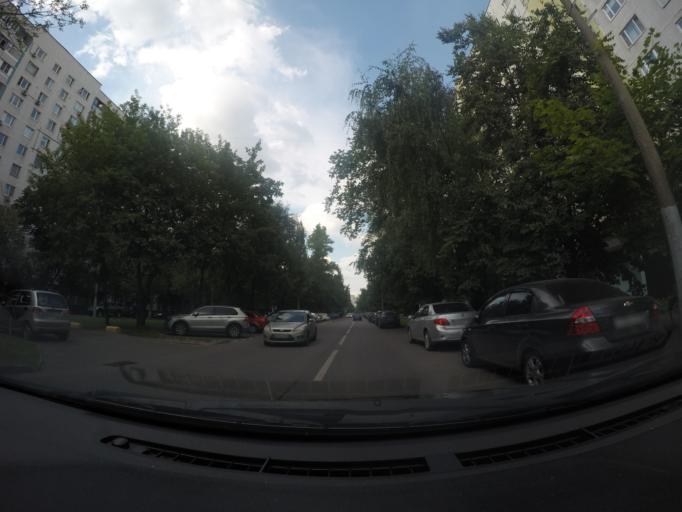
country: RU
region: Moscow
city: Kozeyevo
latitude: 55.8580
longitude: 37.6093
